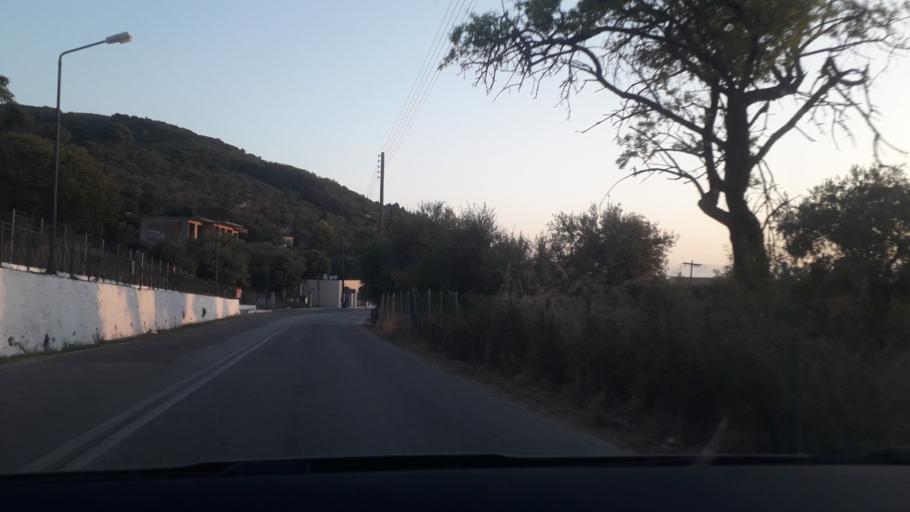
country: GR
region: Ionian Islands
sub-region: Nomos Kerkyras
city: Agios Matthaios
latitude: 39.4868
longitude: 19.9256
